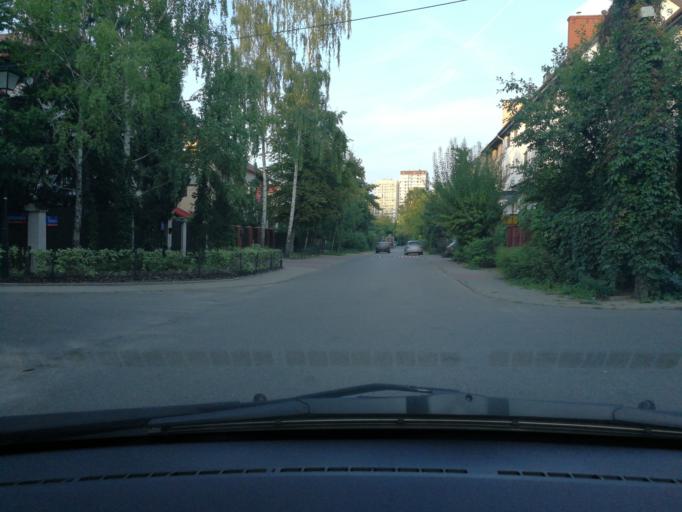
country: PL
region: Masovian Voivodeship
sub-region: Warszawa
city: Zoliborz
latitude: 52.2815
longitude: 20.9672
